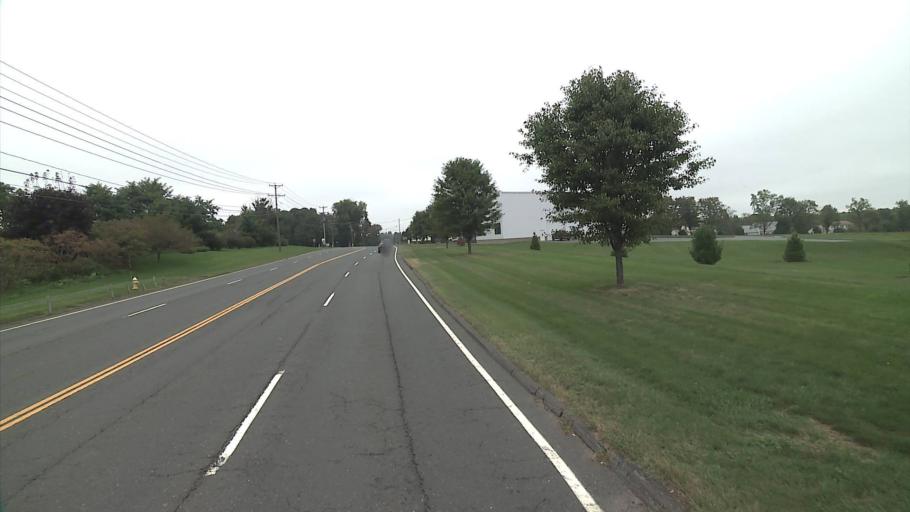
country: US
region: Connecticut
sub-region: Hartford County
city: Suffield Depot
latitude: 41.9606
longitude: -72.6627
